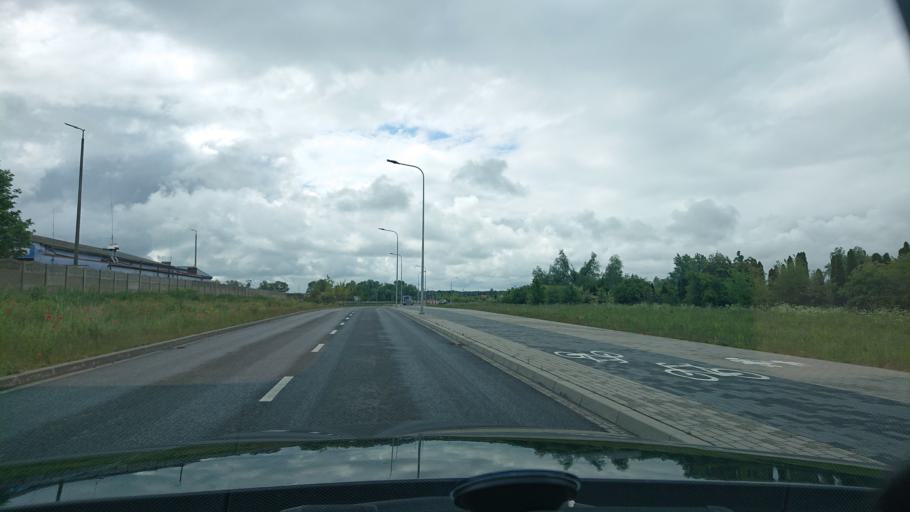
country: PL
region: Greater Poland Voivodeship
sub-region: Powiat gnieznienski
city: Gniezno
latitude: 52.5279
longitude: 17.6228
